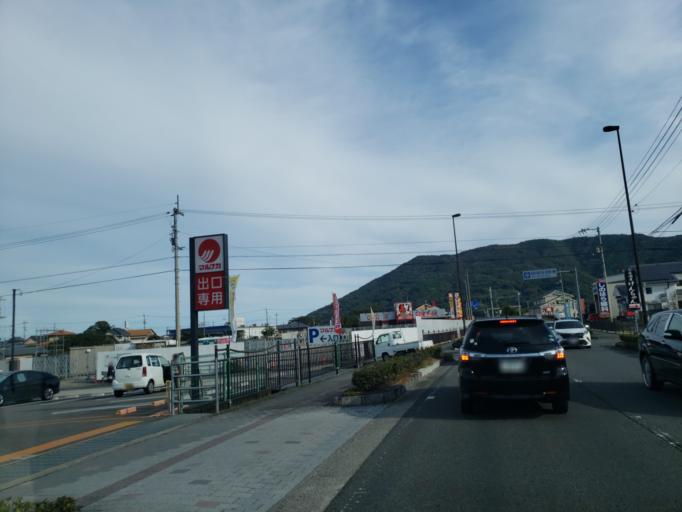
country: JP
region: Tokushima
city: Wakimachi
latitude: 34.0633
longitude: 134.1667
